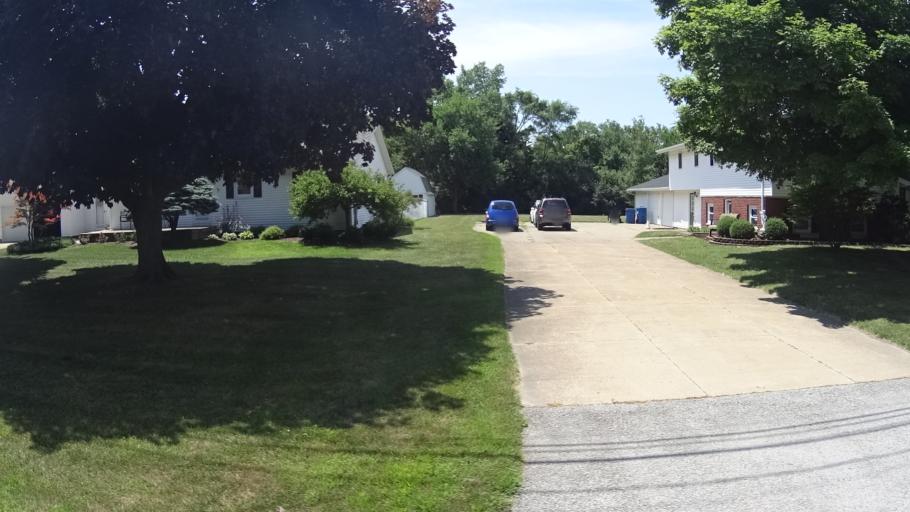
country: US
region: Ohio
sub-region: Erie County
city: Sandusky
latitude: 41.4016
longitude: -82.7882
